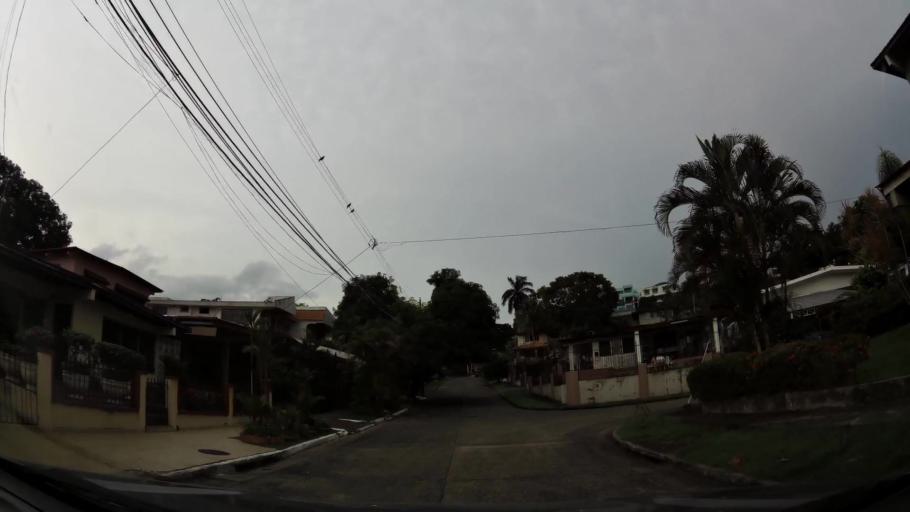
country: PA
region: Panama
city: Panama
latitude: 9.0138
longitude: -79.5241
